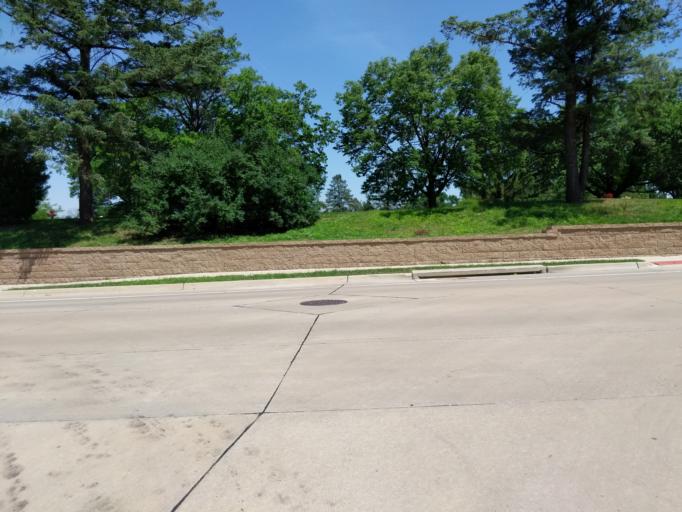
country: US
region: Iowa
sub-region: Linn County
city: Cedar Rapids
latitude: 42.0214
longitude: -91.6387
